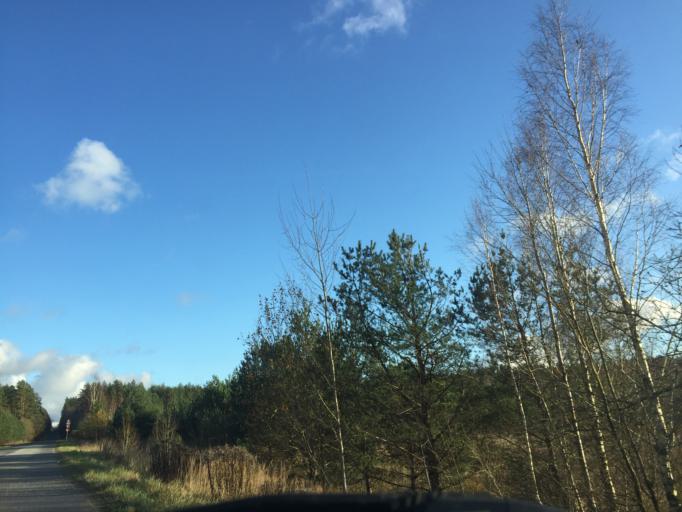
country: LV
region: Sigulda
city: Sigulda
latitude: 57.0870
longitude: 24.7899
